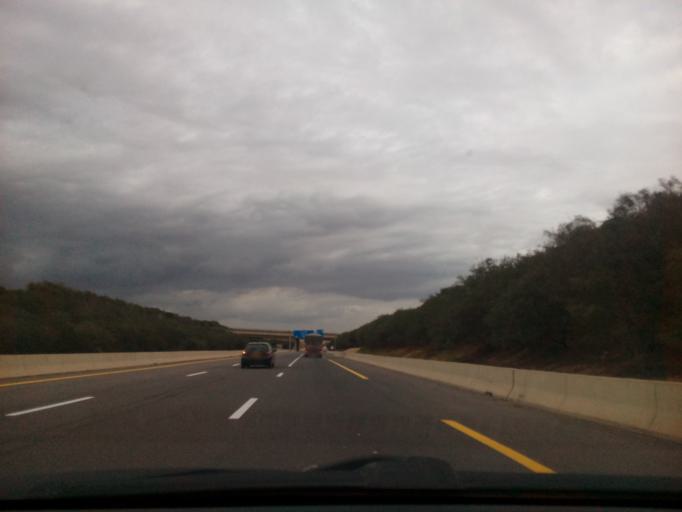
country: DZ
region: Mascara
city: Sig
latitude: 35.5399
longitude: -0.3447
